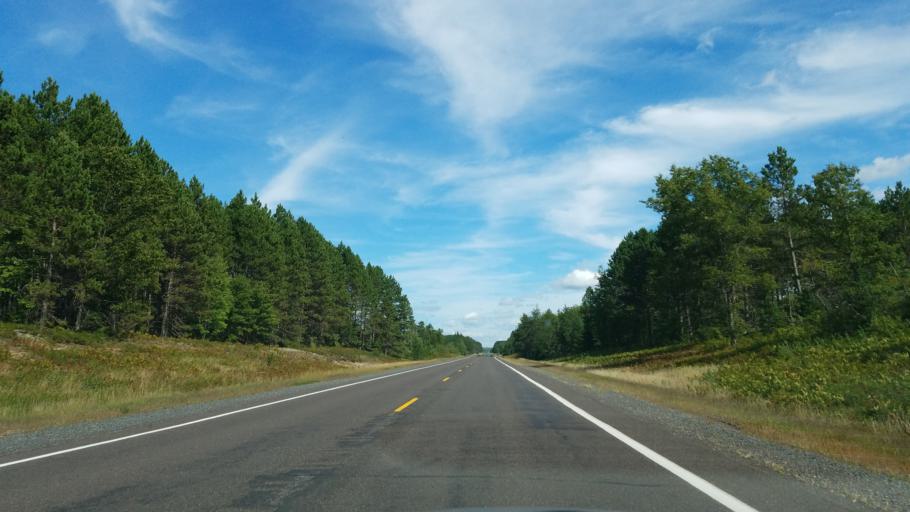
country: US
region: Michigan
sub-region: Baraga County
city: Baraga
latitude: 46.5061
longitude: -88.7546
